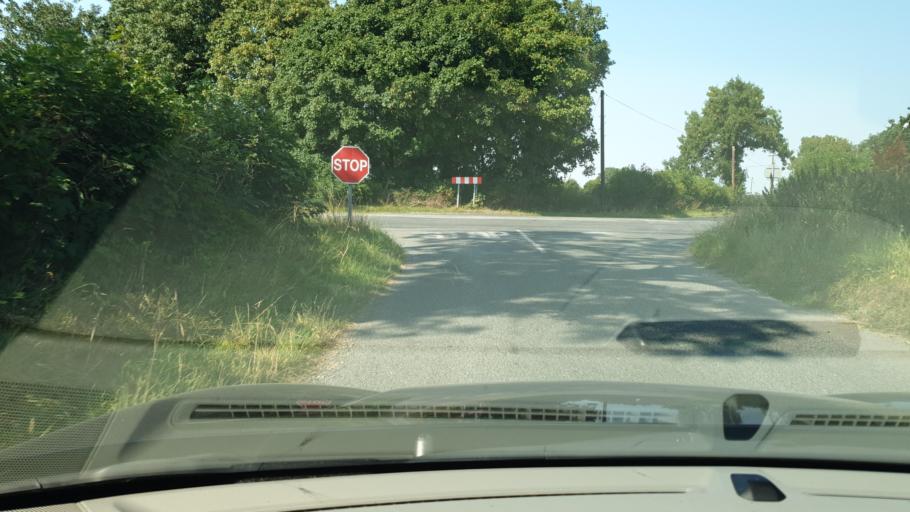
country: IE
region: Leinster
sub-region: An Mhi
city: Athboy
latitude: 53.6358
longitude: -6.9803
